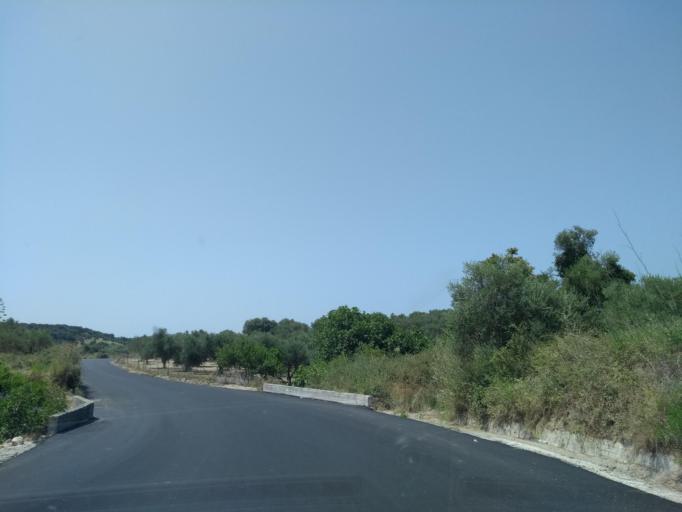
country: GR
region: Crete
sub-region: Nomos Chanias
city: Georgioupolis
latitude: 35.3268
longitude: 24.2999
